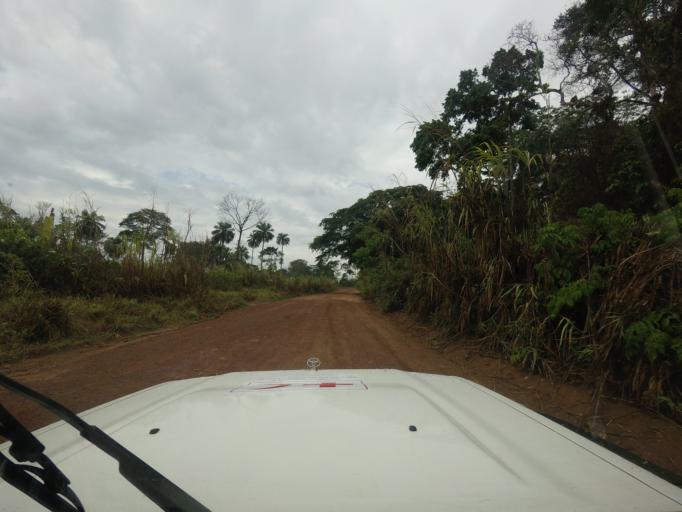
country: SL
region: Eastern Province
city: Buedu
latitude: 8.3443
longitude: -10.1768
